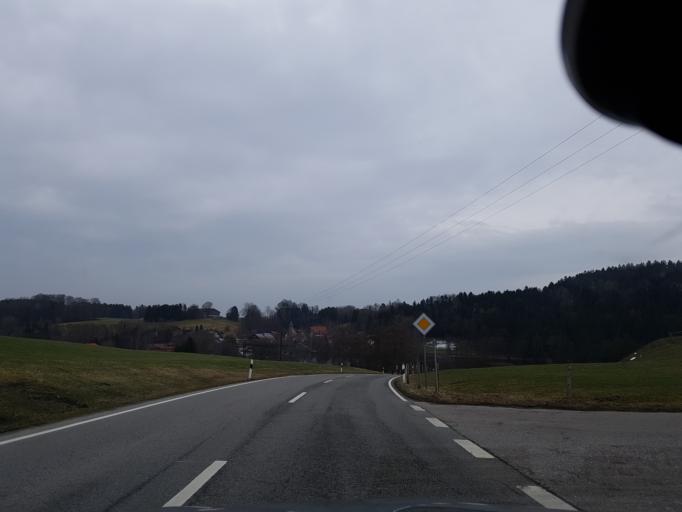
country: DE
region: Bavaria
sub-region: Upper Bavaria
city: Feldkirchen-Westerham
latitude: 47.9406
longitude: 11.8555
